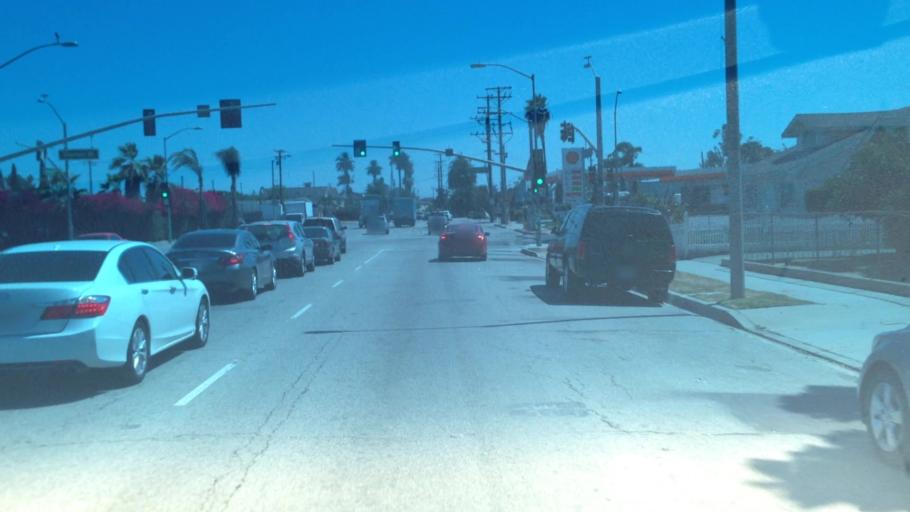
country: US
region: California
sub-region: Los Angeles County
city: Montebello
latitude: 34.0070
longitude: -118.1092
